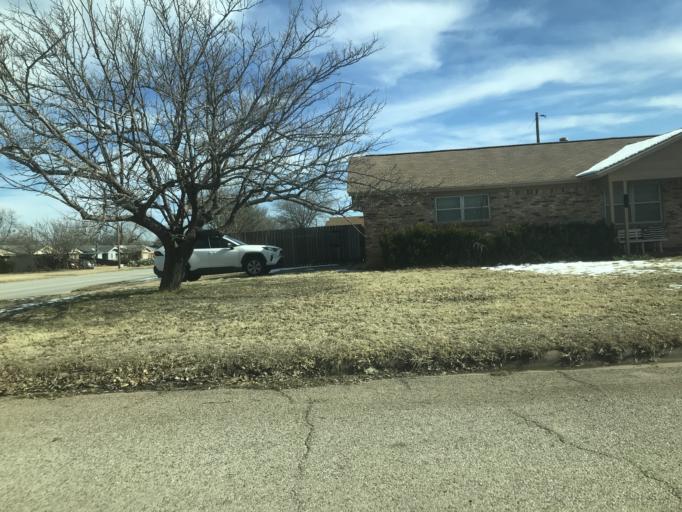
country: US
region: Texas
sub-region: Taylor County
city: Abilene
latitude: 32.4740
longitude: -99.7702
